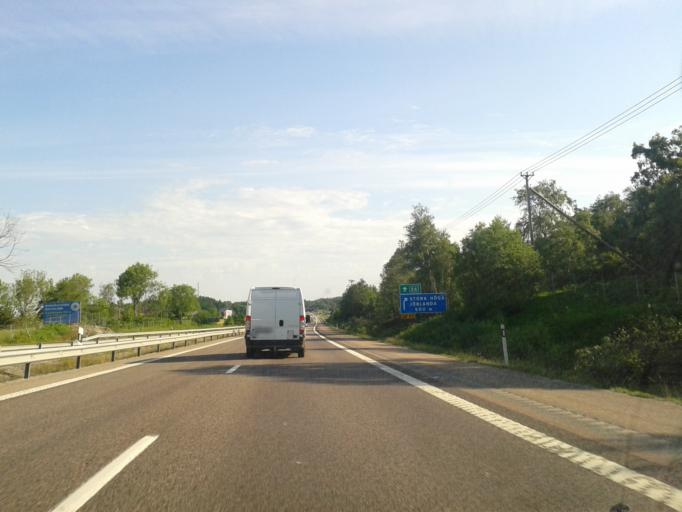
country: SE
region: Vaestra Goetaland
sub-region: Kungalvs Kommun
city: Kode
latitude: 57.9744
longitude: 11.8398
